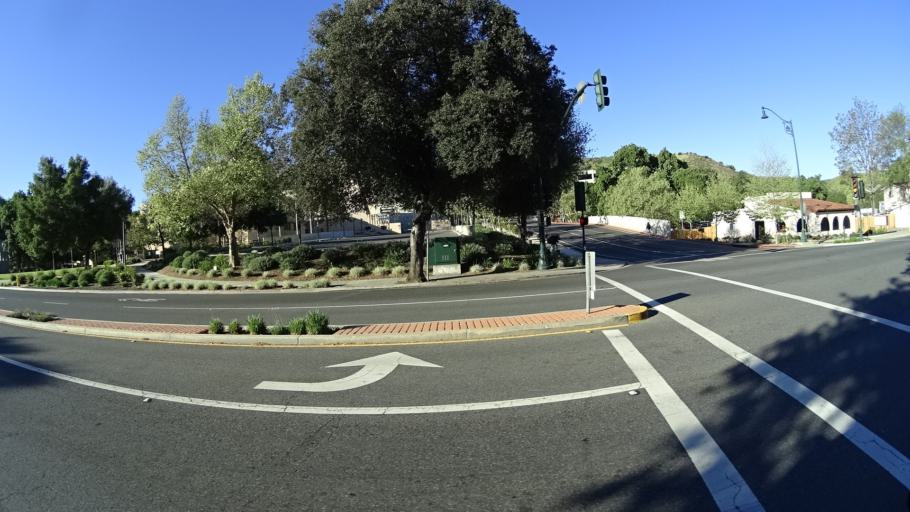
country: US
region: California
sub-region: Ventura County
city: Thousand Oaks
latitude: 34.1759
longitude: -118.8486
